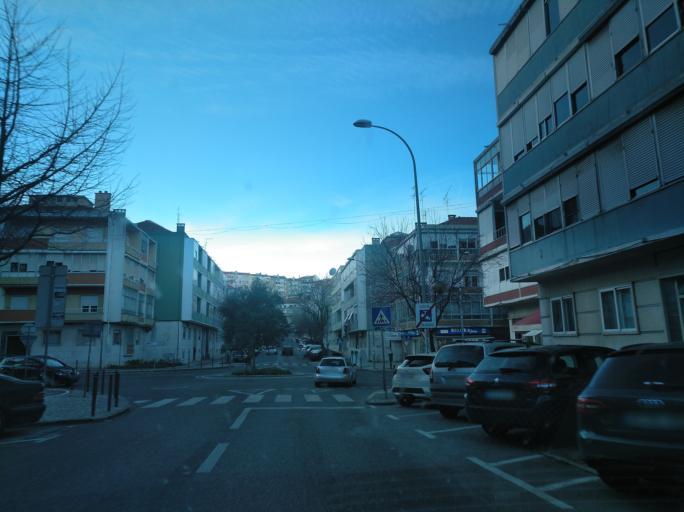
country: PT
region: Lisbon
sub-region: Amadora
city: Amadora
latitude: 38.7443
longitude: -9.2206
